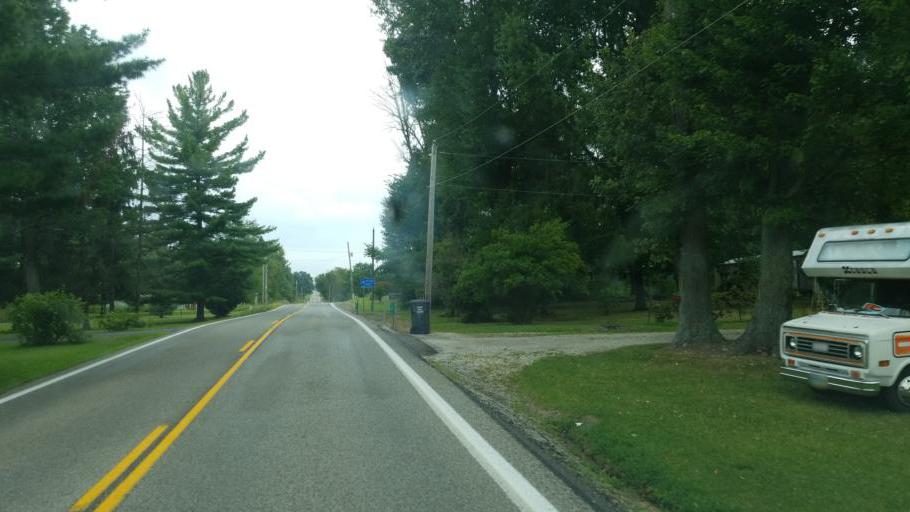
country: US
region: Ohio
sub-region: Morrow County
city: Mount Gilead
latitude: 40.6235
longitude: -82.7658
